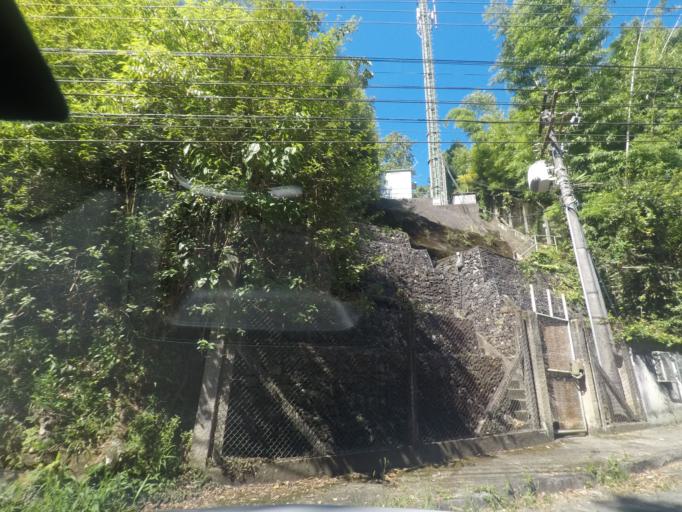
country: BR
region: Rio de Janeiro
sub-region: Petropolis
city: Petropolis
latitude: -22.5118
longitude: -43.1861
